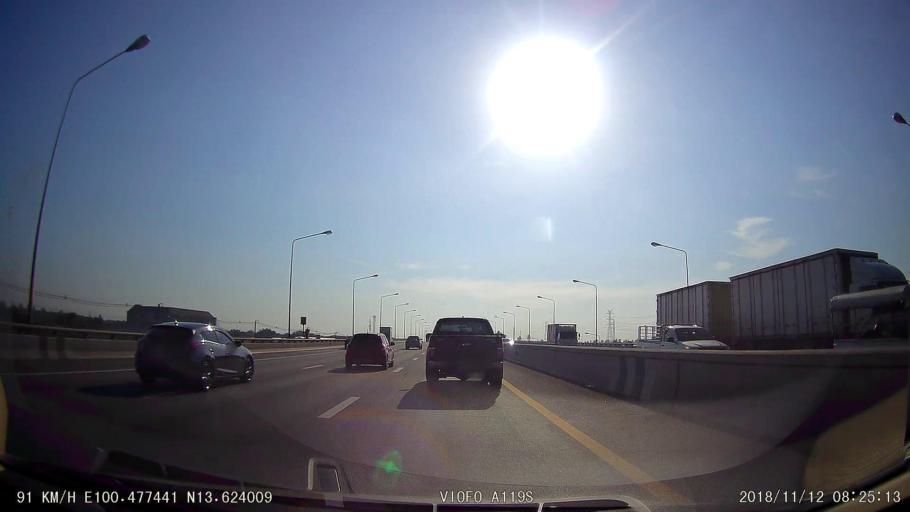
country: TH
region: Bangkok
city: Thung Khru
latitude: 13.6239
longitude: 100.4777
